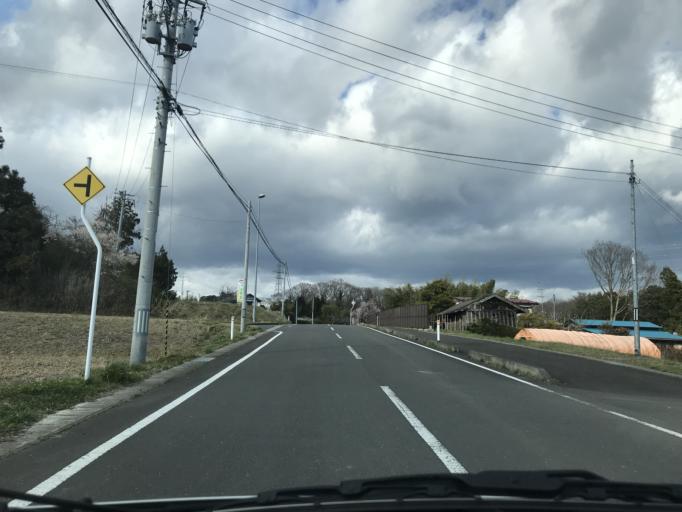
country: JP
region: Miyagi
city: Wakuya
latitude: 38.6238
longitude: 141.2251
